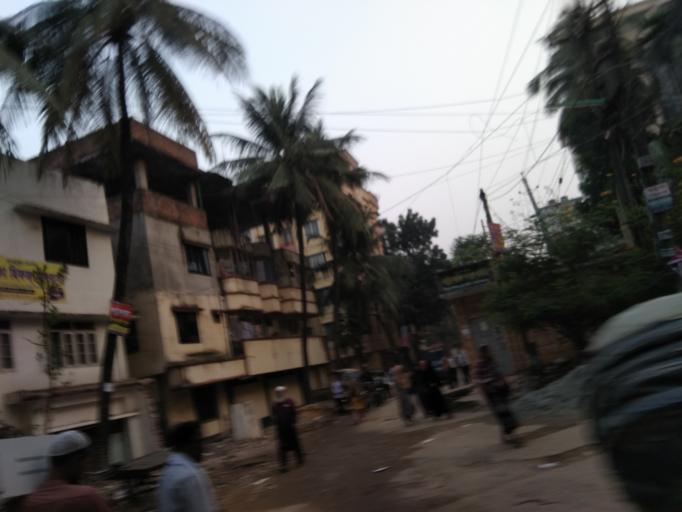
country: BD
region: Dhaka
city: Tungi
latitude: 23.8159
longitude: 90.3678
